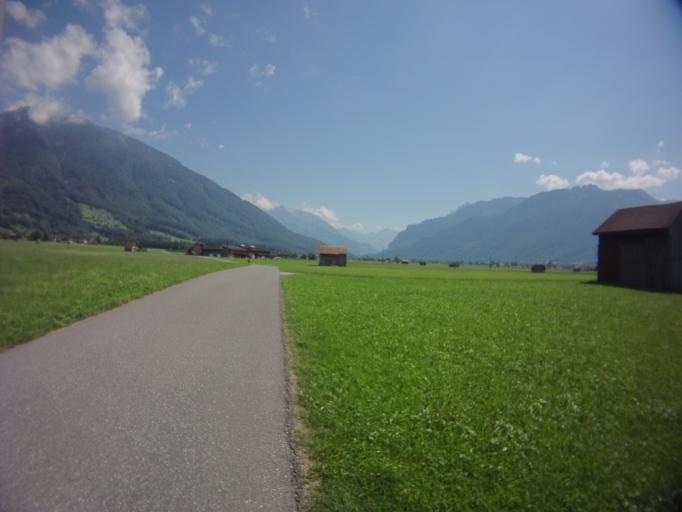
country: CH
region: Saint Gallen
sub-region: Wahlkreis See-Gaster
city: Schanis
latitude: 47.1859
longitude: 9.0377
